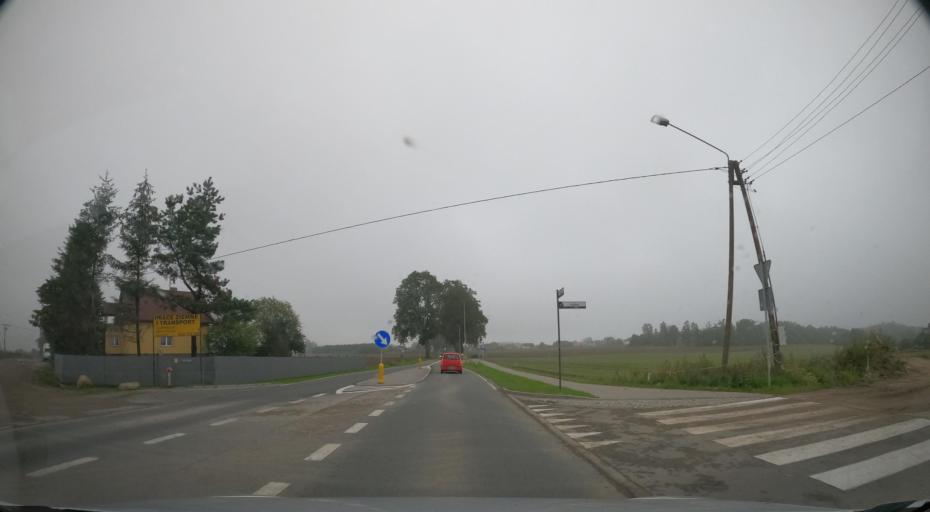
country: PL
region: Pomeranian Voivodeship
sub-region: Powiat wejherowski
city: Bojano
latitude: 54.4513
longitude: 18.3727
